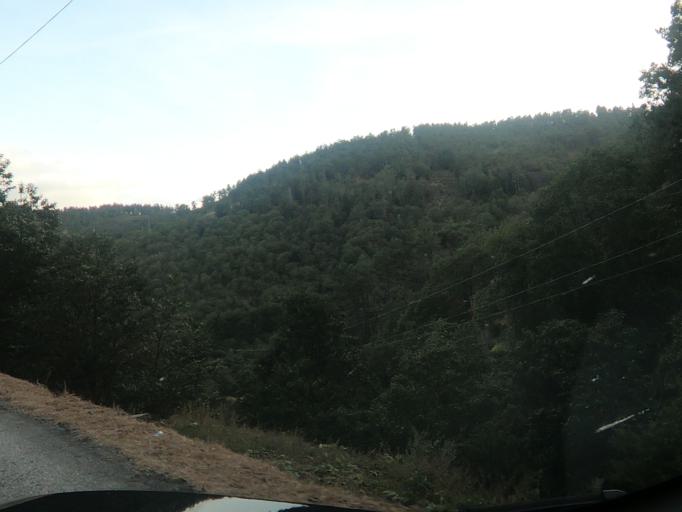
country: PT
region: Vila Real
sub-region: Santa Marta de Penaguiao
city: Santa Marta de Penaguiao
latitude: 41.2454
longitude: -7.8501
